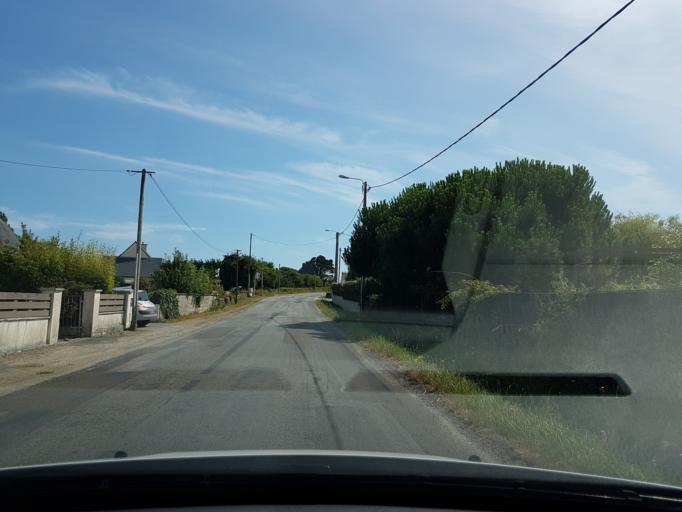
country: FR
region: Brittany
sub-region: Departement du Morbihan
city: Etel
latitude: 47.6743
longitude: -3.2206
